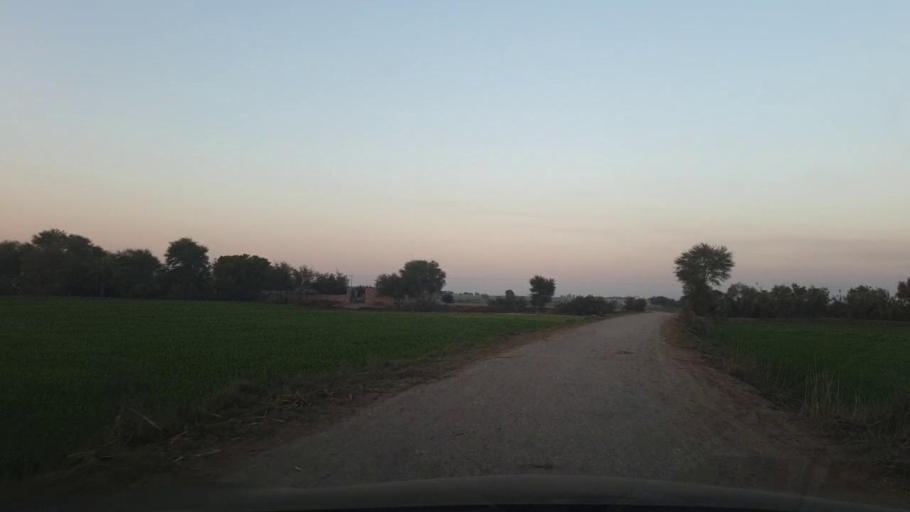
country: PK
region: Sindh
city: Ubauro
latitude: 28.1737
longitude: 69.6352
